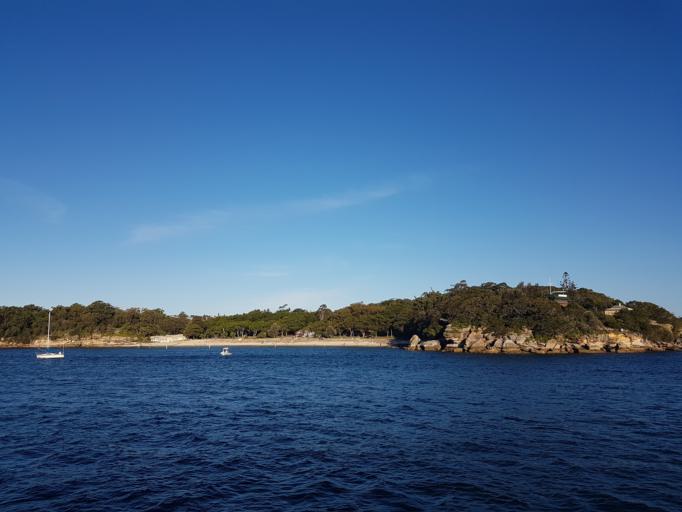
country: AU
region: New South Wales
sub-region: Woollahra
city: Point Piper
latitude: -33.8492
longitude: 151.2632
